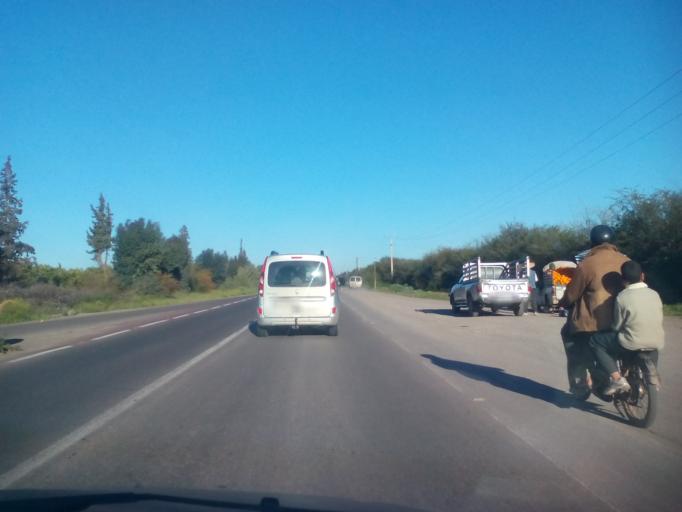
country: MA
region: Marrakech-Tensift-Al Haouz
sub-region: Marrakech
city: Marrakesh
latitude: 31.6297
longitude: -8.1435
